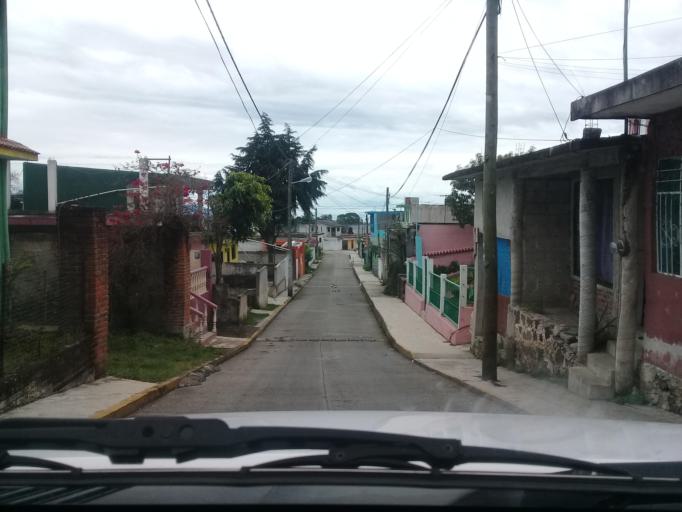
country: MX
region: Veracruz
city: Rafael Lucio
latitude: 19.5929
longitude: -96.9887
